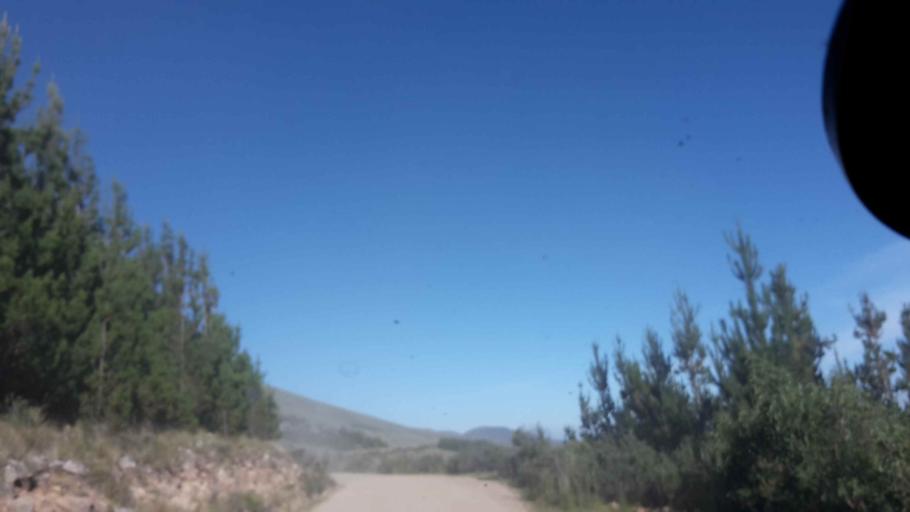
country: BO
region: Cochabamba
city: Arani
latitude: -17.7154
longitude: -65.6718
